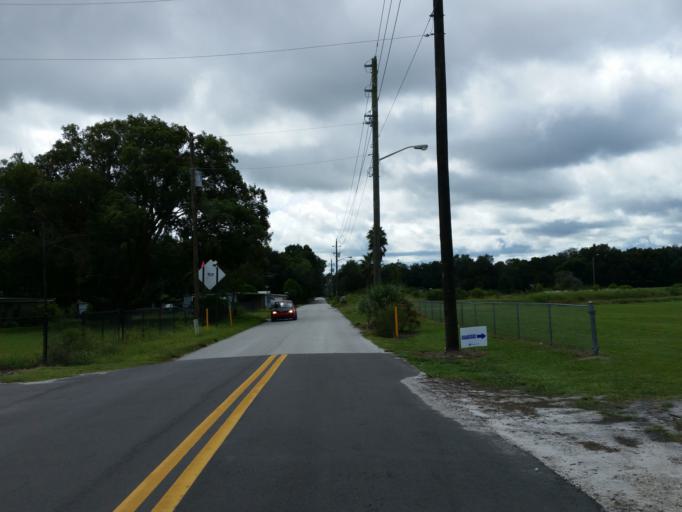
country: US
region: Florida
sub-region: Pasco County
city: Zephyrhills West
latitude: 28.2214
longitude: -82.2378
